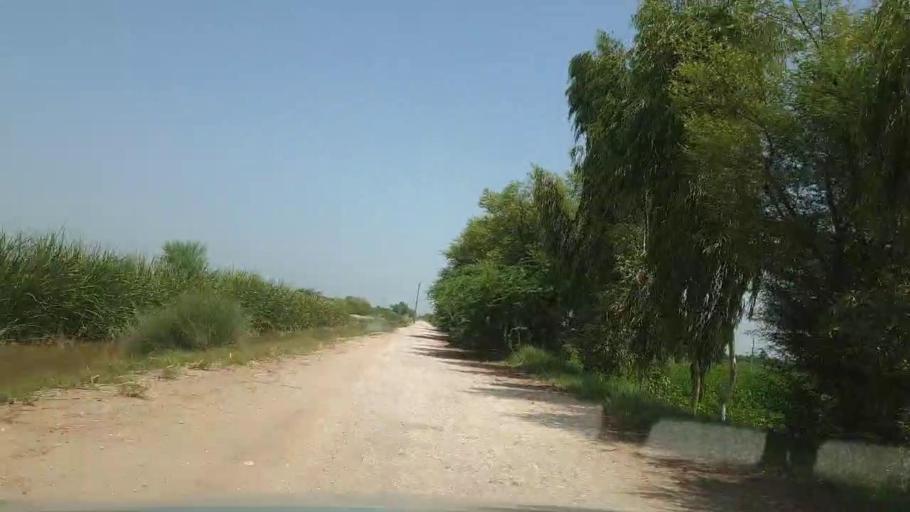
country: PK
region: Sindh
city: Rohri
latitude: 27.6364
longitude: 69.1013
